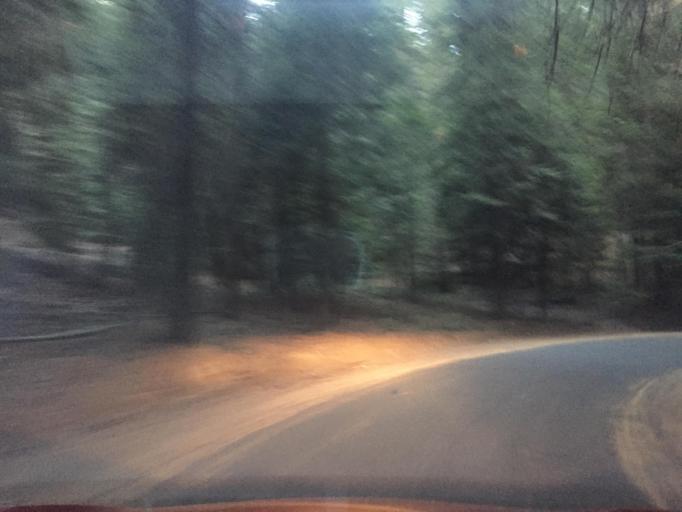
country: US
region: California
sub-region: Tulare County
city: Three Rivers
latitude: 36.4646
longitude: -118.6764
